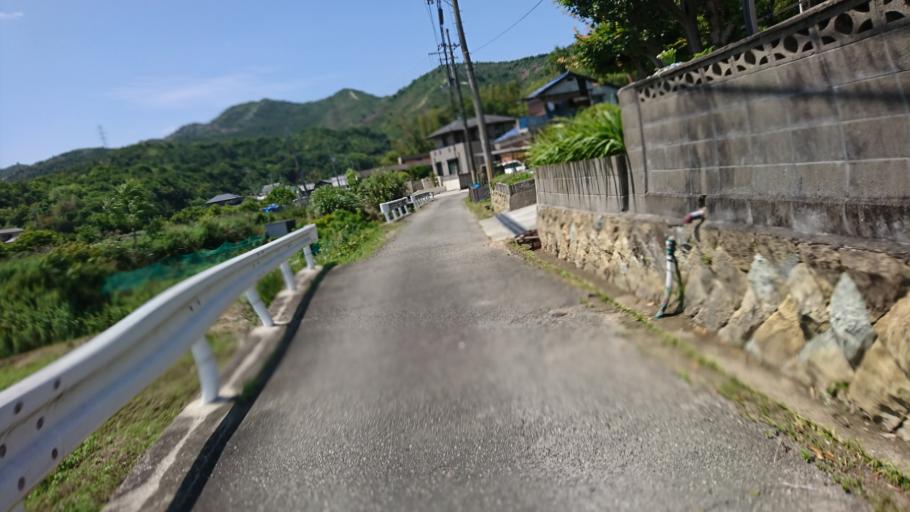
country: JP
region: Hyogo
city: Kakogawacho-honmachi
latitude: 34.8074
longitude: 134.7872
